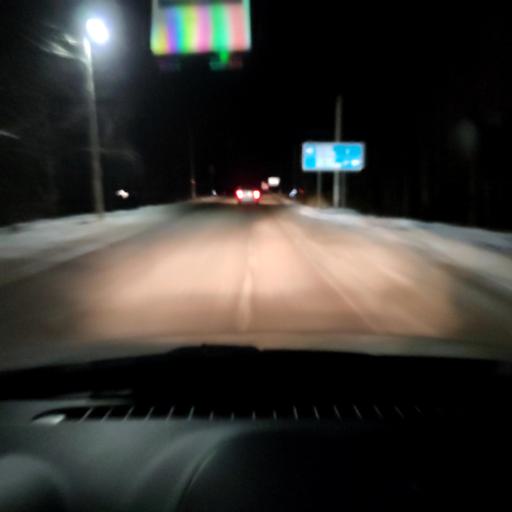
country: RU
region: Tatarstan
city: Vysokaya Gora
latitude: 55.8028
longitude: 49.3767
